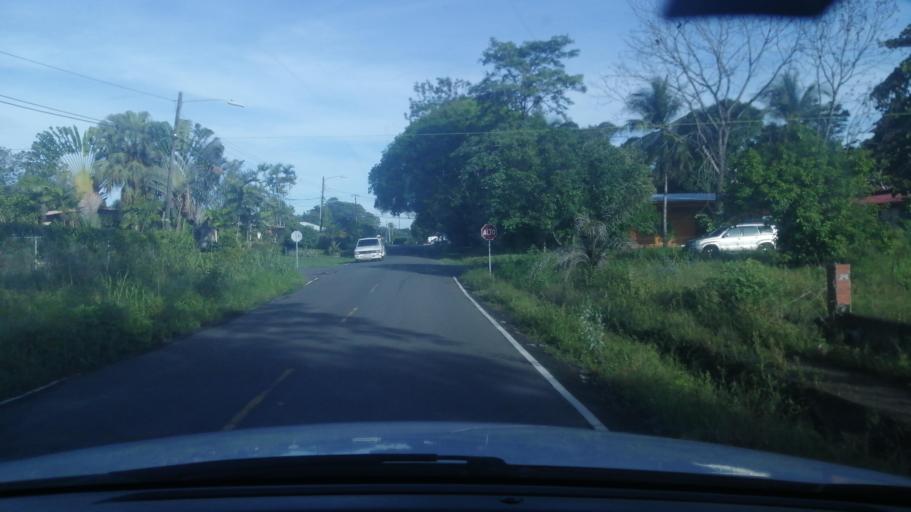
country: PA
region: Chiriqui
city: Mata del Nance
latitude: 8.4483
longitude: -82.4223
